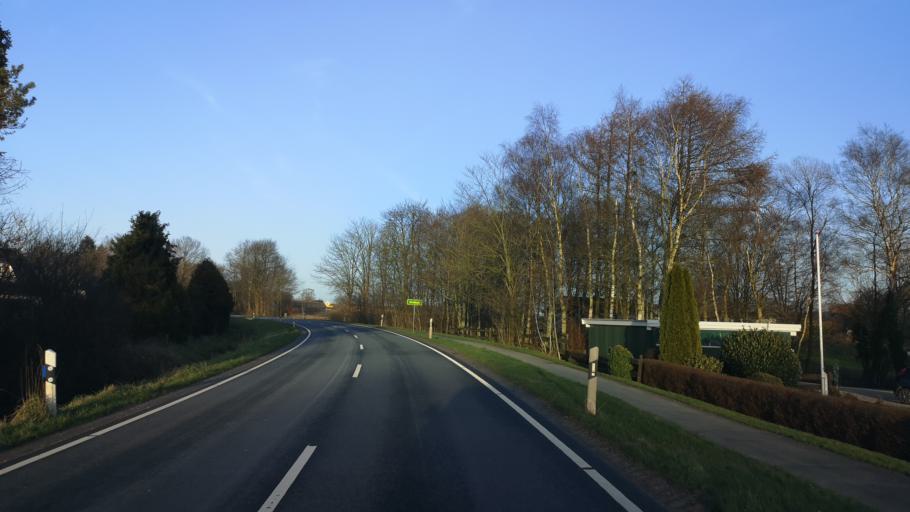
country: DE
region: Schleswig-Holstein
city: Grosssolt
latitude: 54.6968
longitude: 9.5163
